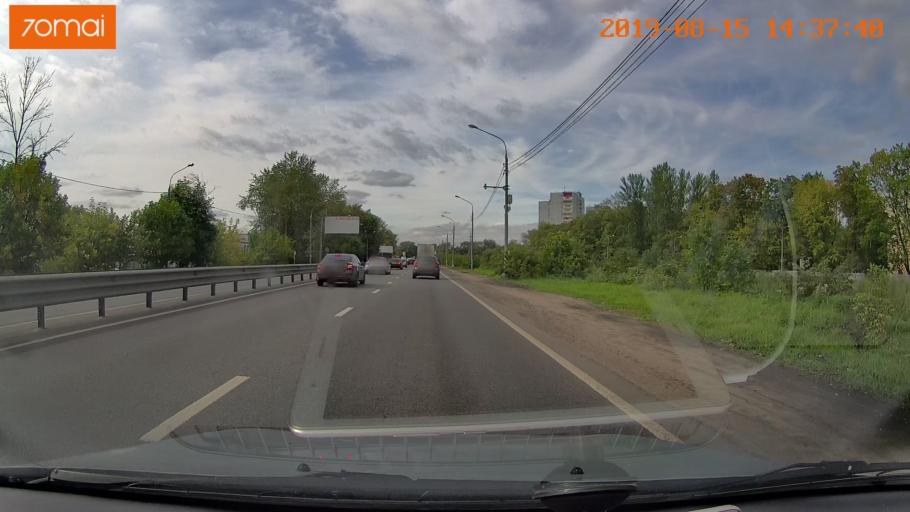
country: RU
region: Moskovskaya
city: Tomilino
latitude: 55.6540
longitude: 37.9245
